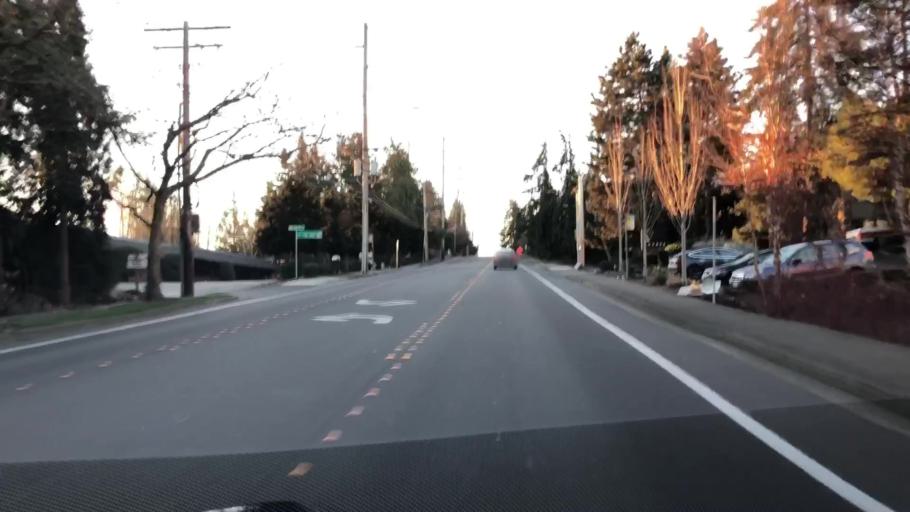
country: US
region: Washington
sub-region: King County
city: Bellevue
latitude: 47.6306
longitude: -122.1856
